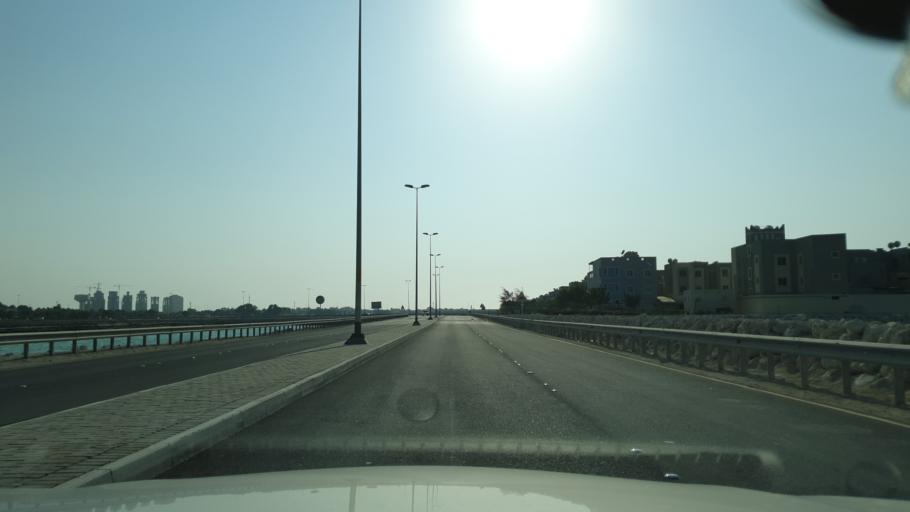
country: BH
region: Manama
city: Jidd Hafs
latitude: 26.2294
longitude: 50.4589
